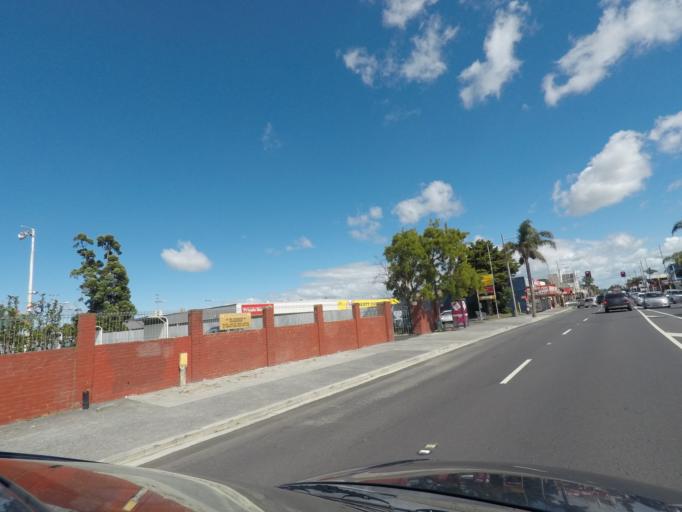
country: NZ
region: Auckland
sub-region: Auckland
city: Wiri
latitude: -36.9717
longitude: 174.8625
